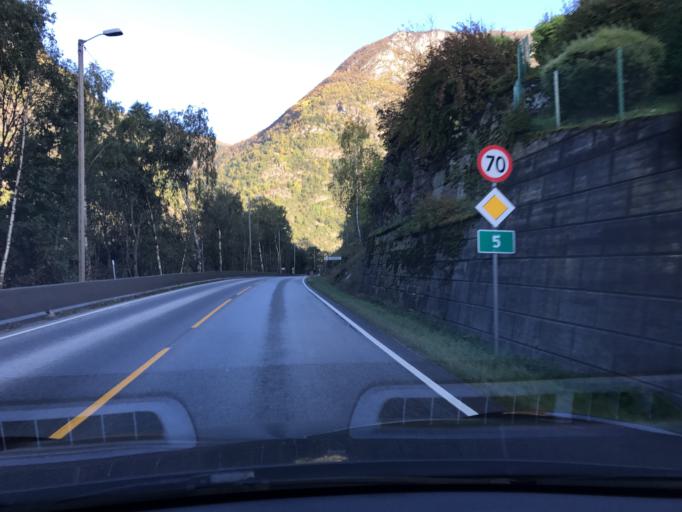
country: NO
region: Sogn og Fjordane
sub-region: Laerdal
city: Laerdalsoyri
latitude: 61.1007
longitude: 7.5033
